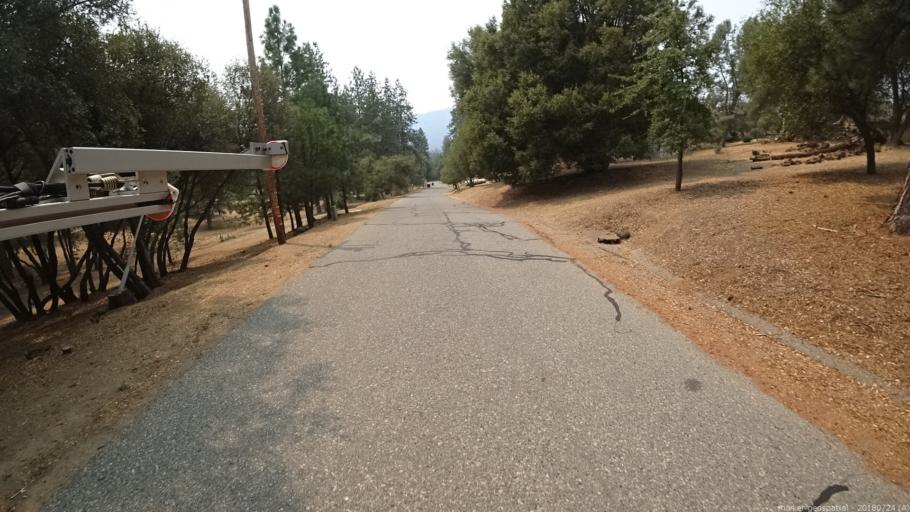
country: US
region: California
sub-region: Madera County
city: Oakhurst
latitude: 37.3152
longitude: -119.6037
